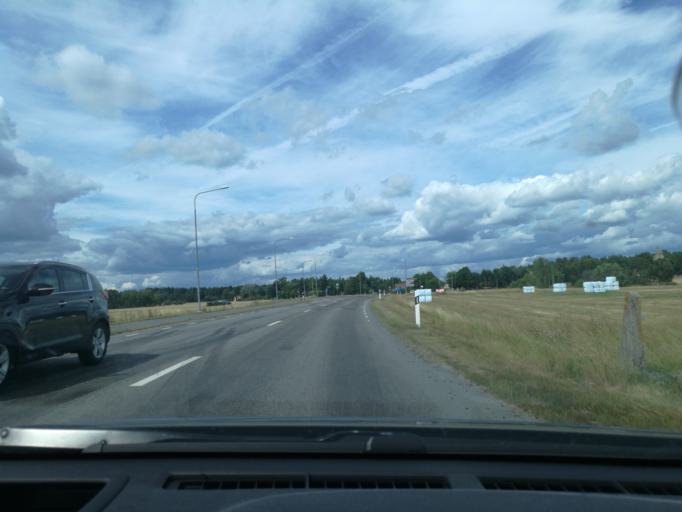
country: SE
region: Stockholm
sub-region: Sigtuna Kommun
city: Rosersberg
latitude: 59.5891
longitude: 17.8922
